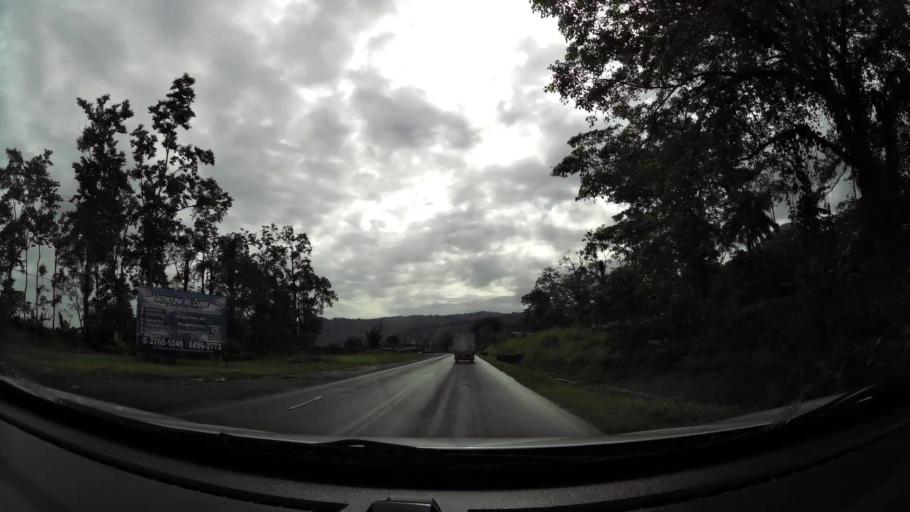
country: CR
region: Limon
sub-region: Canton de Siquirres
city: Siquirres
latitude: 10.0983
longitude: -83.5152
